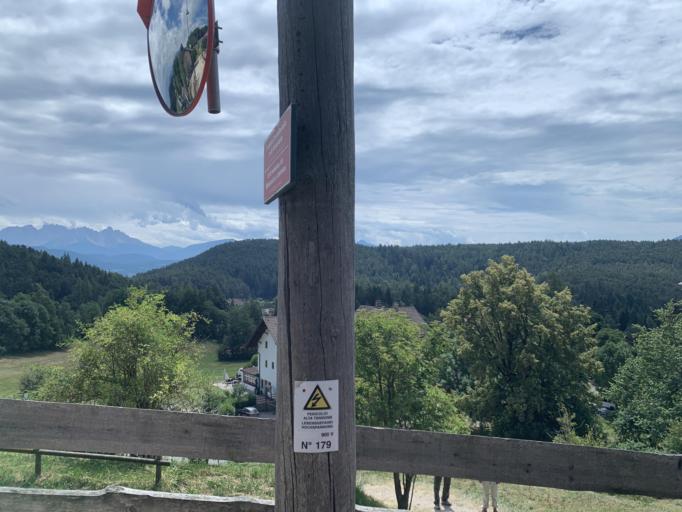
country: IT
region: Trentino-Alto Adige
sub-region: Bolzano
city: Soprabolzano
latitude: 46.5258
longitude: 11.4243
